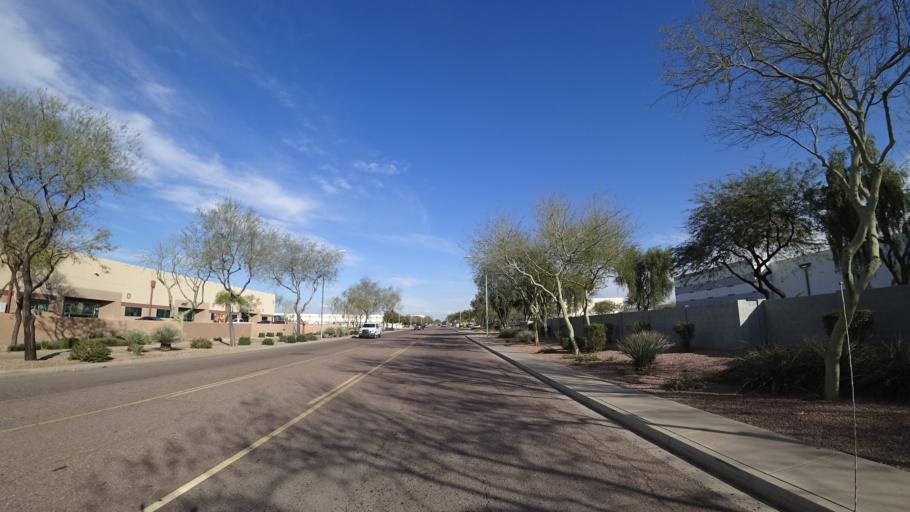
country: US
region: Arizona
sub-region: Maricopa County
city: Tolleson
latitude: 33.4587
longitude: -112.2180
